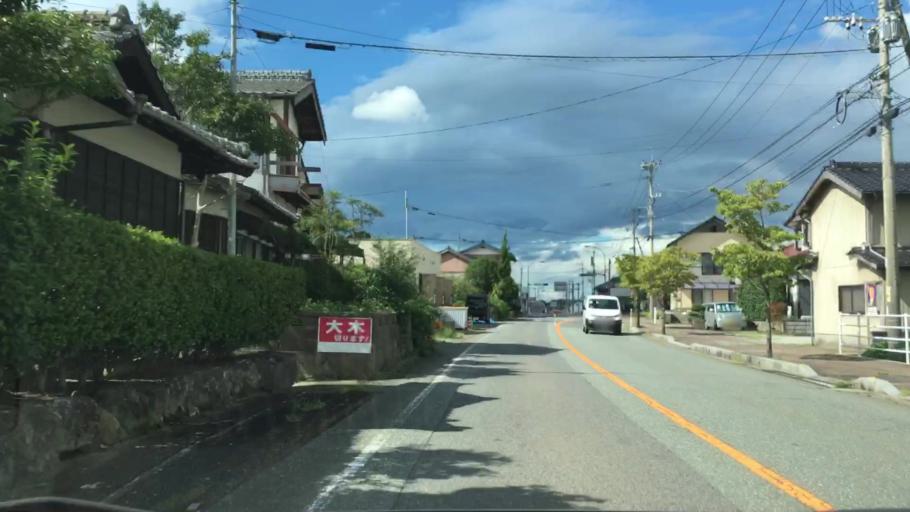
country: JP
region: Saga Prefecture
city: Imaricho-ko
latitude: 33.1945
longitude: 129.8507
